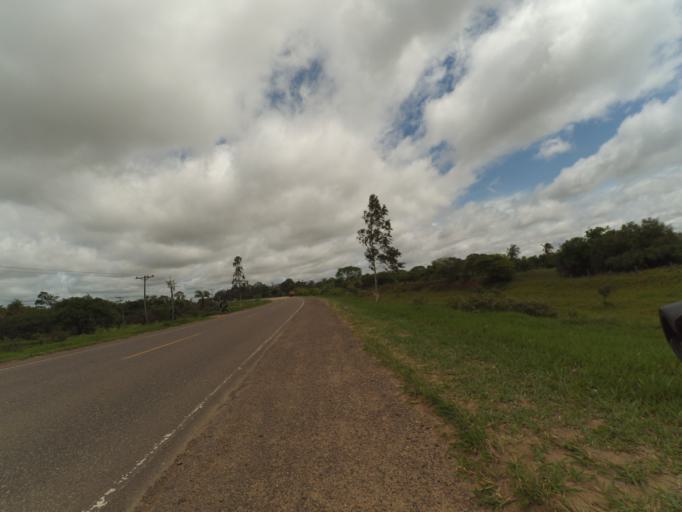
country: BO
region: Santa Cruz
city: Santa Rita
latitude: -17.9080
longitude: -63.2516
